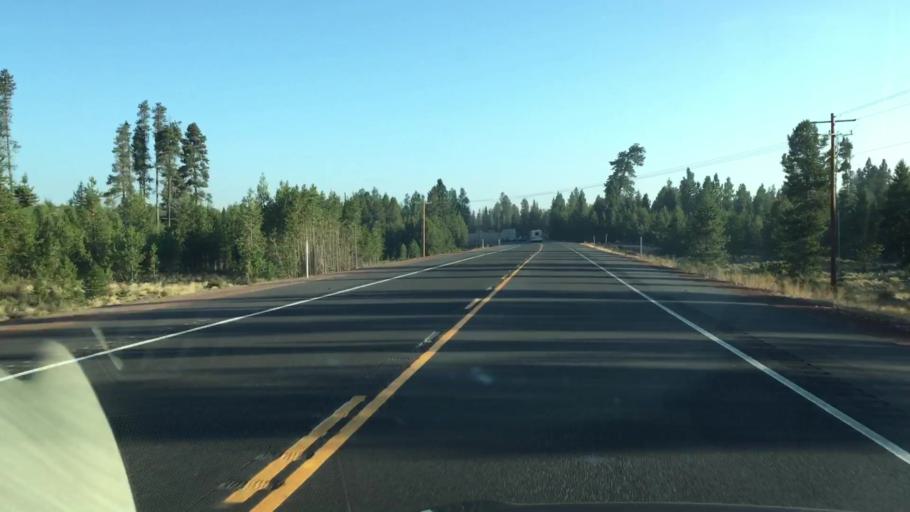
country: US
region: Oregon
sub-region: Deschutes County
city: La Pine
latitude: 43.2045
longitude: -121.7793
